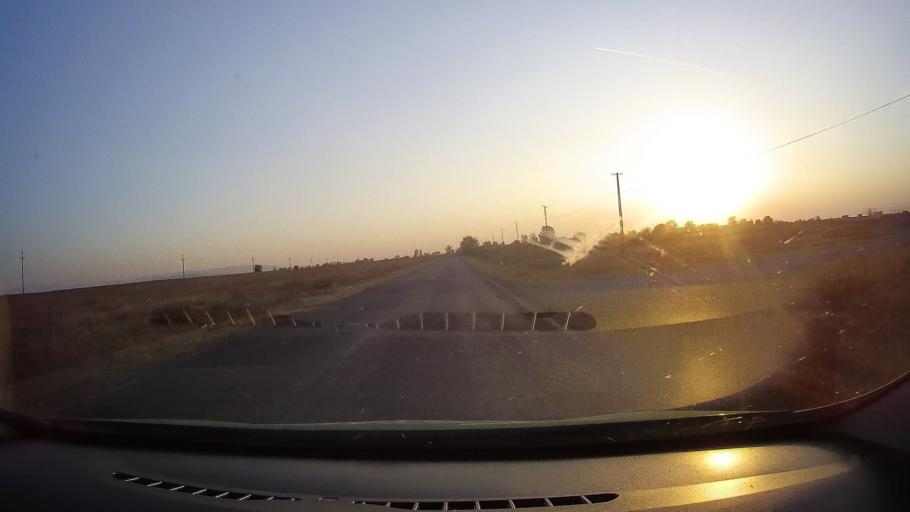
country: RO
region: Arad
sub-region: Comuna Sicula
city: Sicula
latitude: 46.4269
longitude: 21.7534
